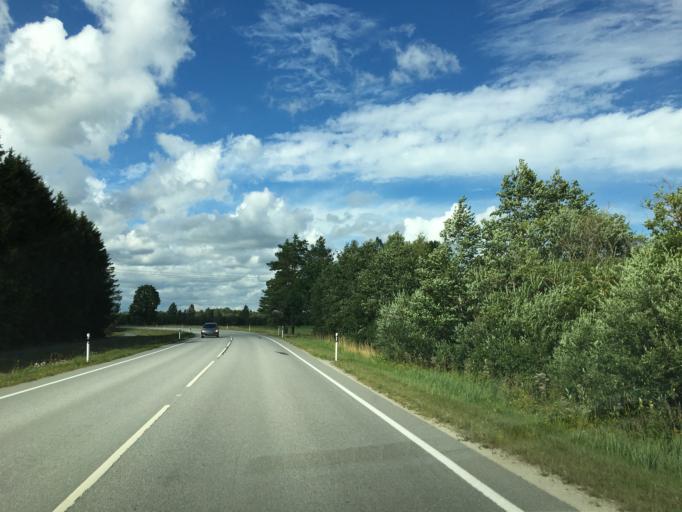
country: EE
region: Paernumaa
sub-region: Vaendra vald (alev)
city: Vandra
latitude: 58.6378
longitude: 25.0999
